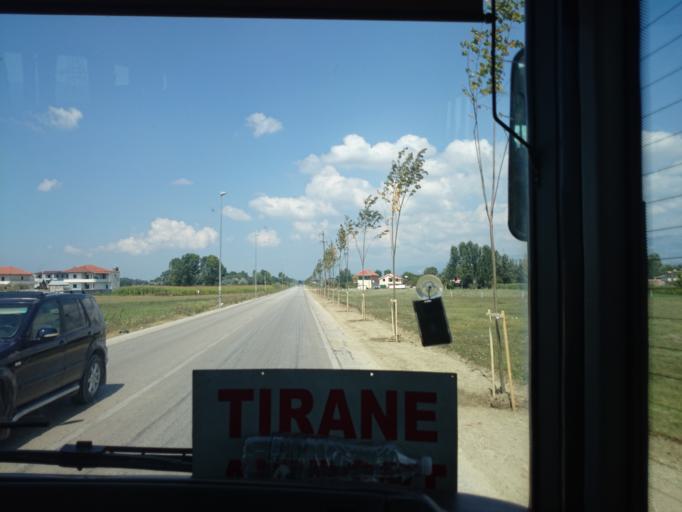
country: AL
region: Tirane
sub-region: Rrethi i Tiranes
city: Berxull
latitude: 41.3881
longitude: 19.7040
